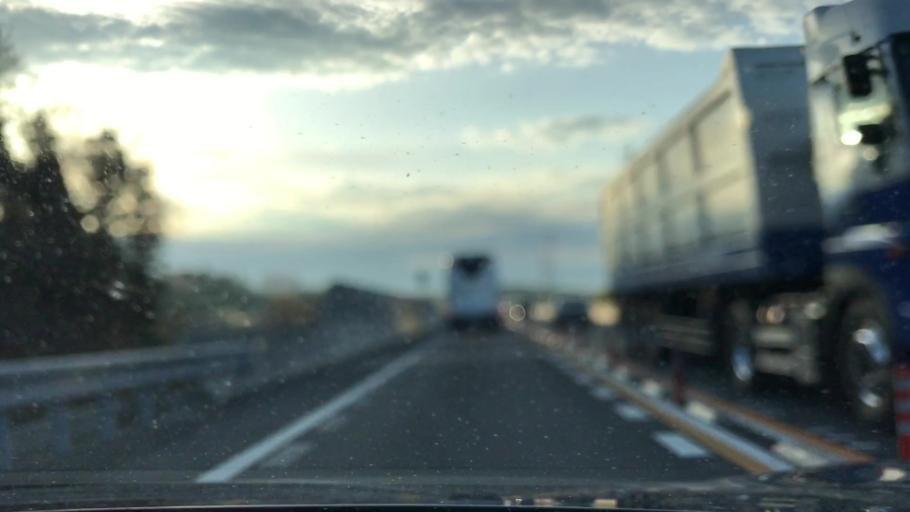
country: JP
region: Ibaraki
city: Ami
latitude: 35.9881
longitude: 140.2246
